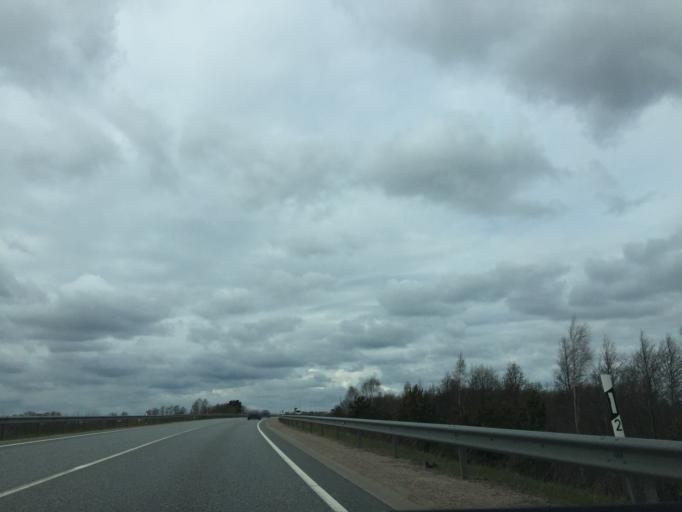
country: LV
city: Tireli
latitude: 56.9286
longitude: 23.6210
